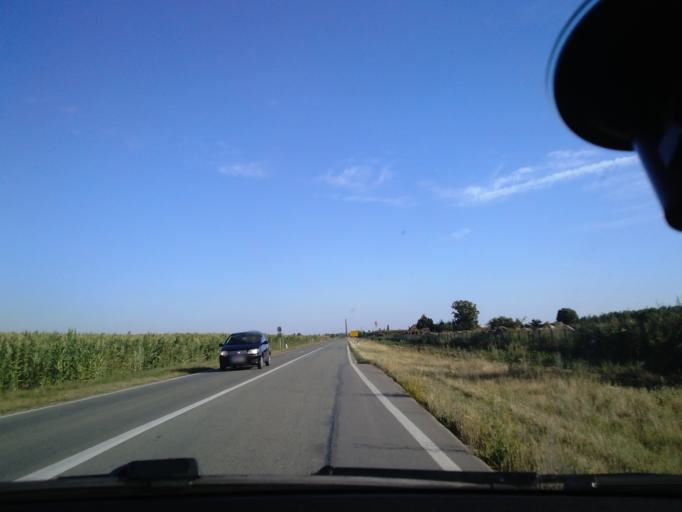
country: RS
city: Doroslovo
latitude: 45.5802
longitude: 19.1896
